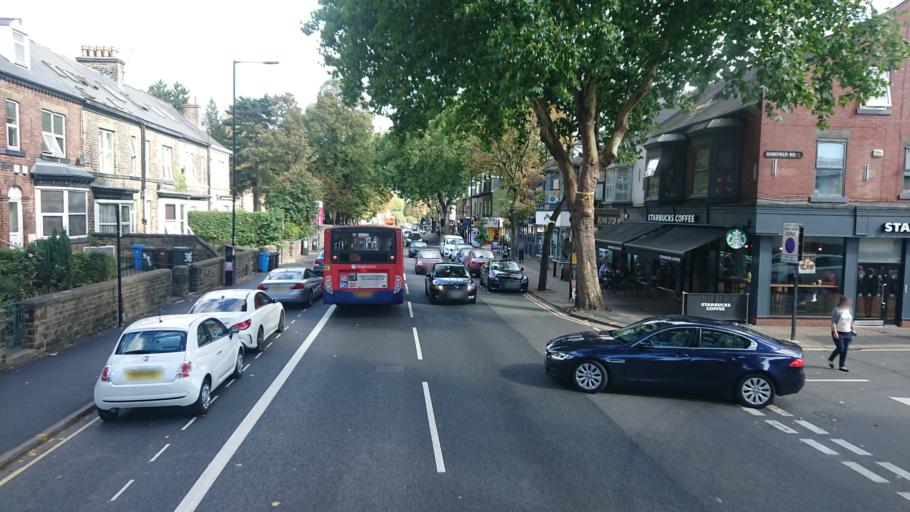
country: GB
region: England
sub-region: Sheffield
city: Sheffield
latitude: 53.3729
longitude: -1.4867
